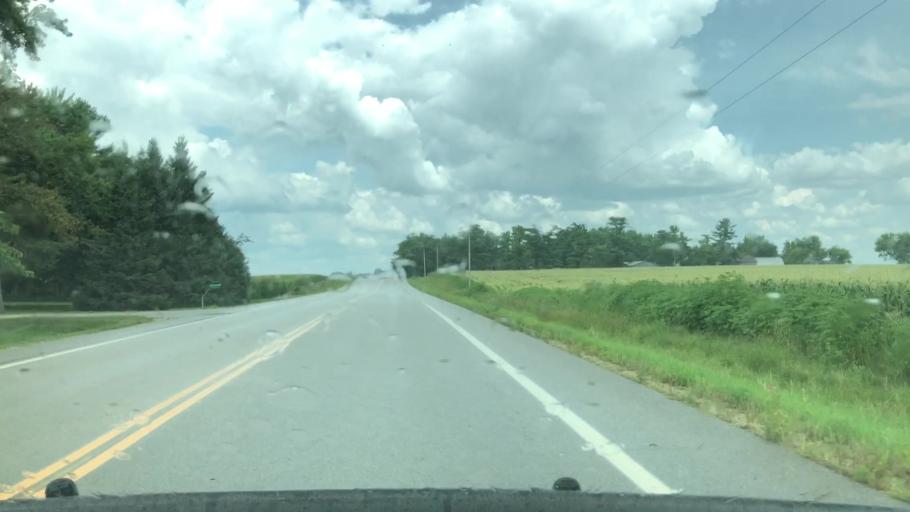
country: US
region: Minnesota
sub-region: Olmsted County
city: Stewartville
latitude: 43.8820
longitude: -92.5285
